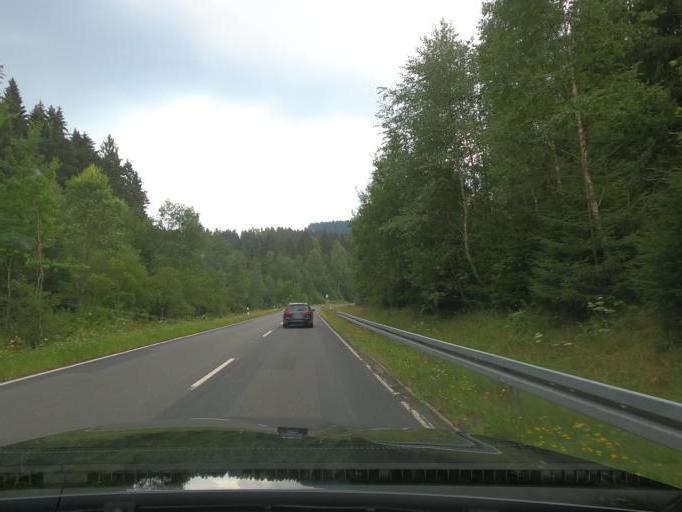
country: DE
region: Lower Saxony
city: Wildemann
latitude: 51.8425
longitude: 10.2684
